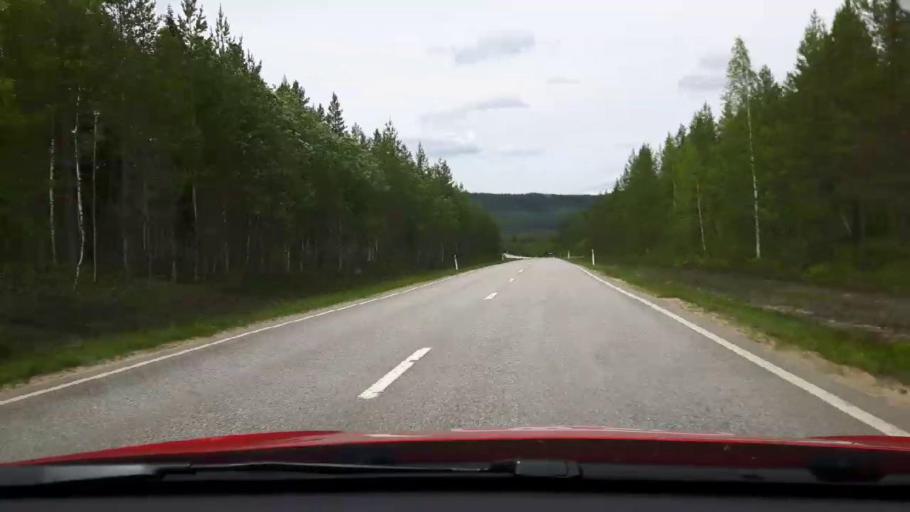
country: SE
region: Jaemtland
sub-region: Harjedalens Kommun
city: Sveg
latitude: 62.0859
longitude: 14.2514
